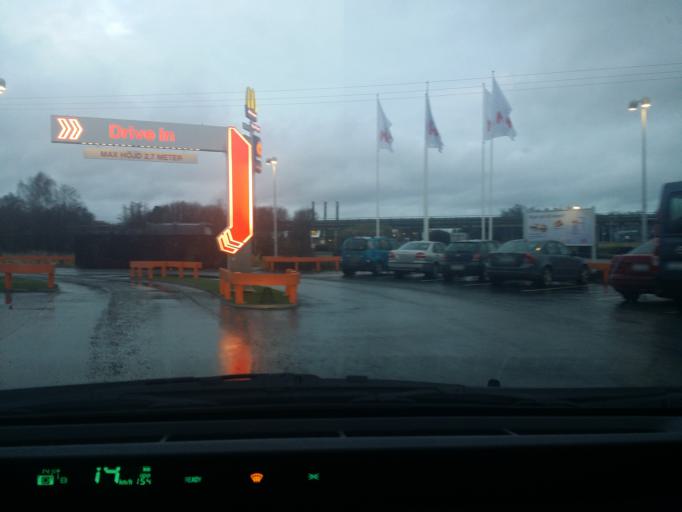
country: SE
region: Soedermanland
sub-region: Eskilstuna Kommun
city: Torshalla
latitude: 59.3920
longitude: 16.4663
